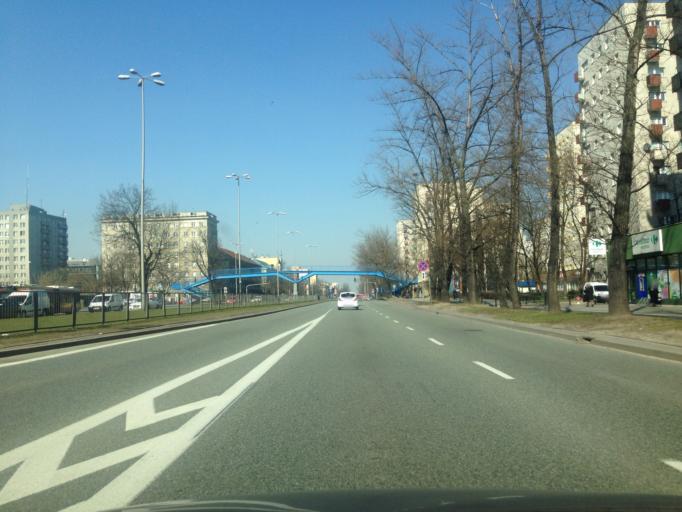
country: PL
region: Masovian Voivodeship
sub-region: Warszawa
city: Mokotow
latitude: 52.2008
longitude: 21.0504
